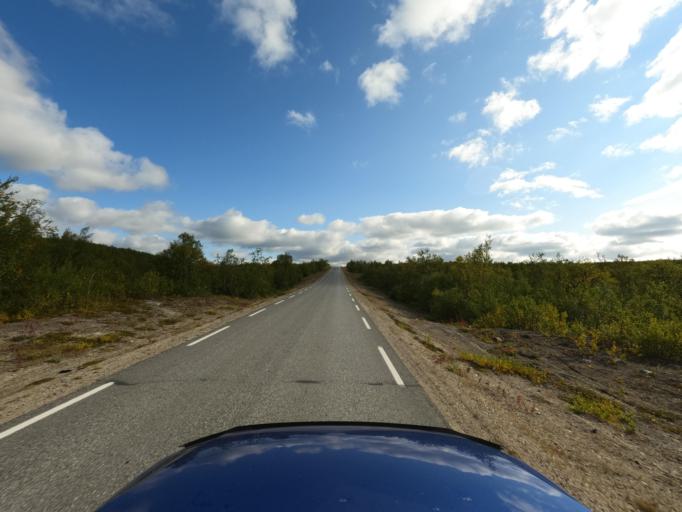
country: NO
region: Finnmark Fylke
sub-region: Porsanger
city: Lakselv
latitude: 69.3909
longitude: 24.5151
